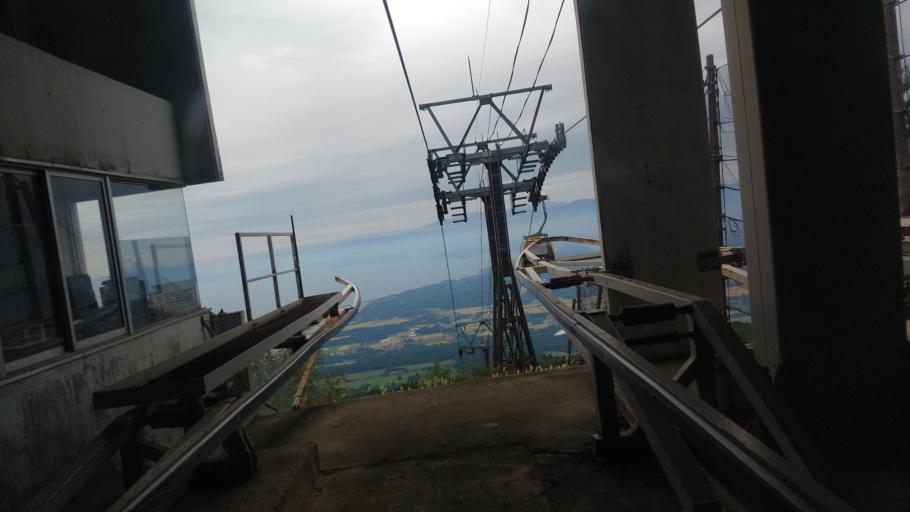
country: JP
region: Fukushima
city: Inawashiro
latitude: 37.5936
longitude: 140.0630
